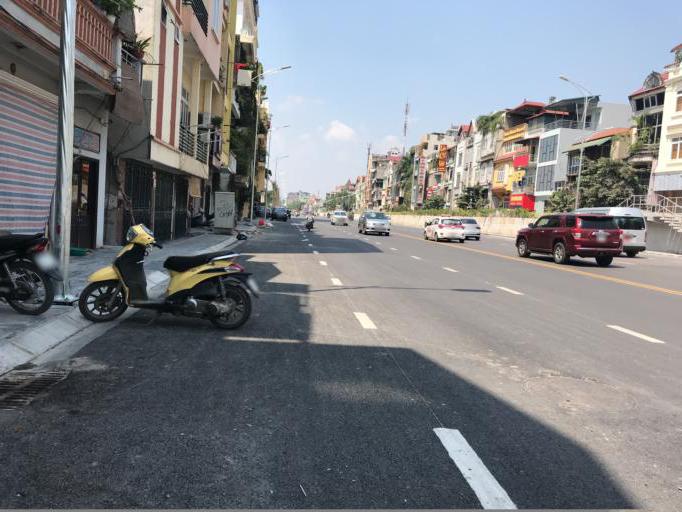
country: VN
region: Ha Noi
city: Hoan Kiem
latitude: 21.0546
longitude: 105.8369
